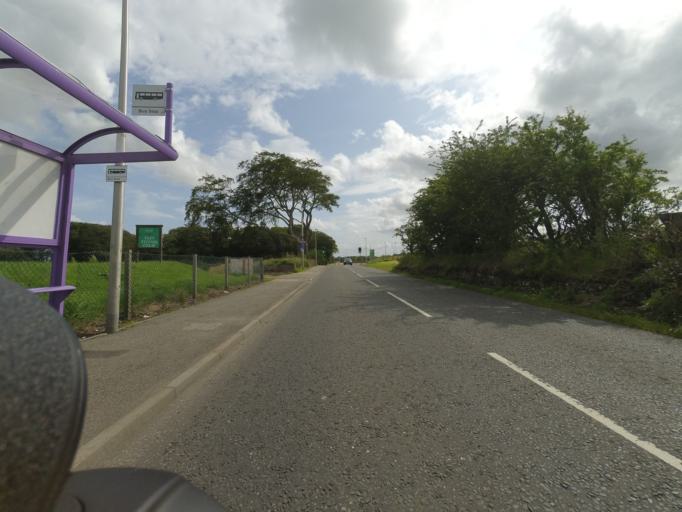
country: GB
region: Scotland
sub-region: Highland
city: Tain
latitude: 57.8055
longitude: -4.0470
